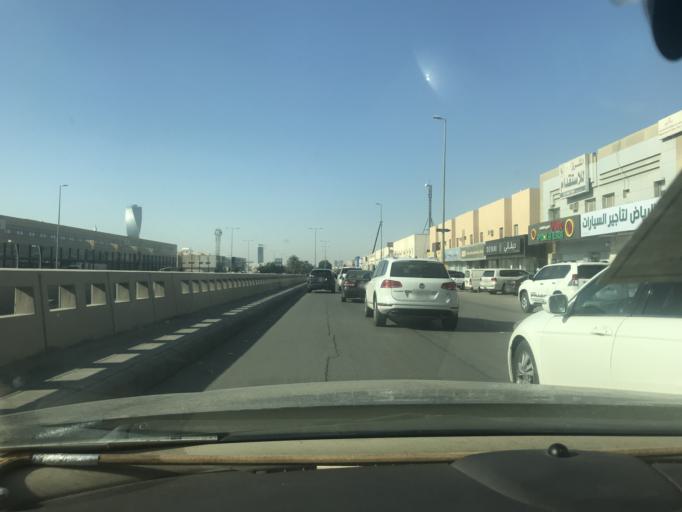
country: SA
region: Ar Riyad
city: Riyadh
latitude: 24.7530
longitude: 46.6752
